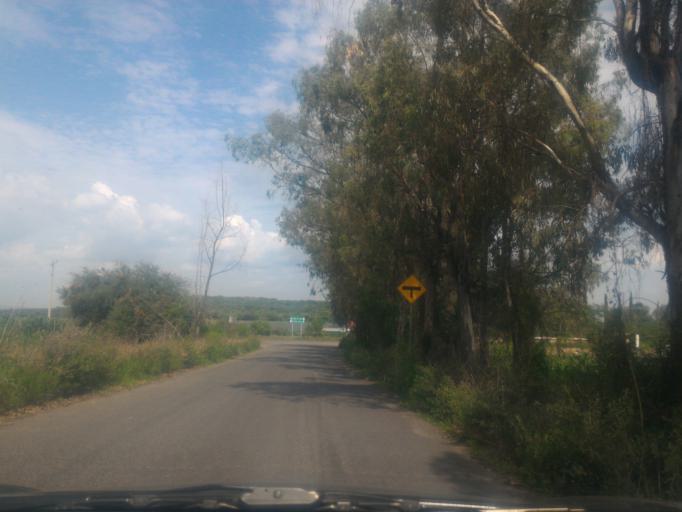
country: MX
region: Guanajuato
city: Ciudad Manuel Doblado
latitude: 20.8349
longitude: -102.0039
